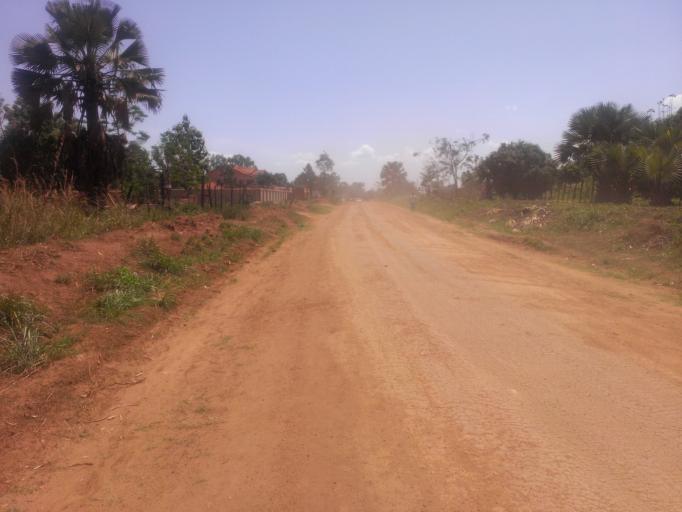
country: UG
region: Northern Region
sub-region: Gulu District
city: Gulu
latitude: 2.7844
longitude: 32.2944
